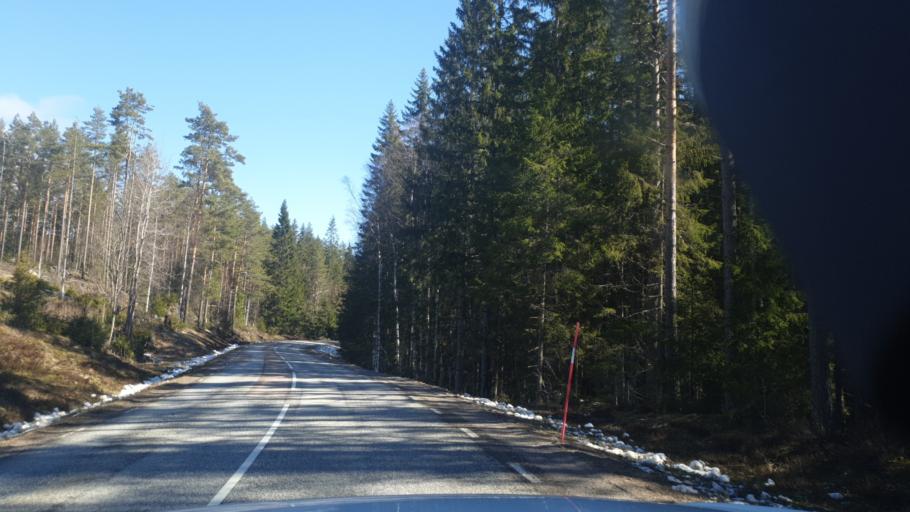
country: SE
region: Vaermland
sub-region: Eda Kommun
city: Amotfors
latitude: 59.6011
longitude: 12.3124
